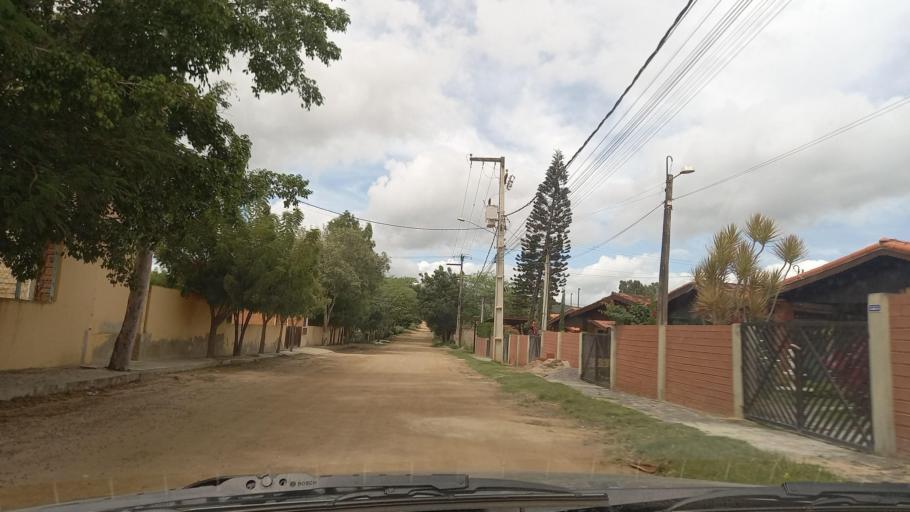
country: BR
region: Pernambuco
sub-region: Gravata
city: Gravata
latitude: -8.1933
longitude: -35.5856
